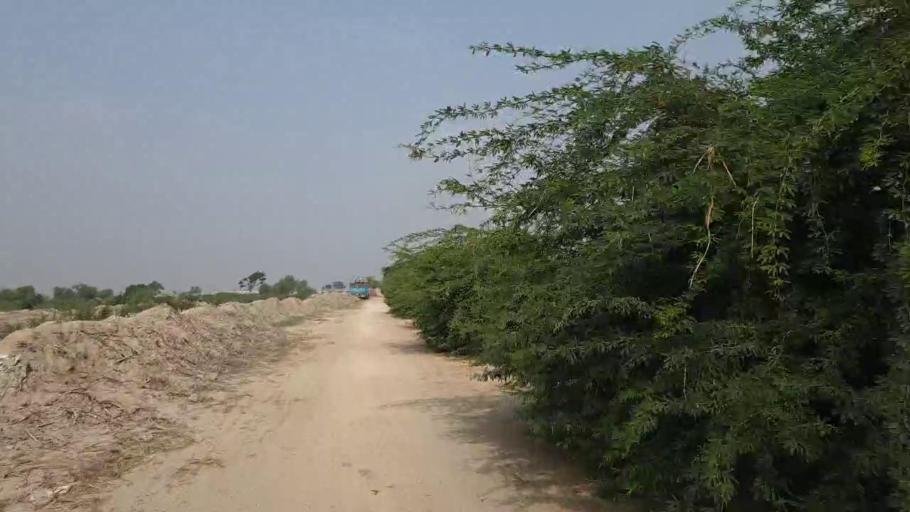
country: PK
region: Sindh
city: Kario
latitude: 24.7786
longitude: 68.5217
